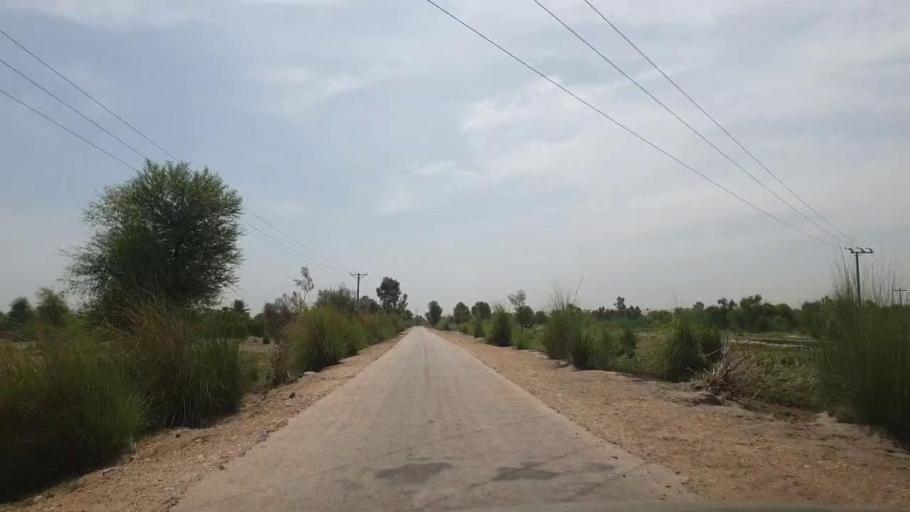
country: PK
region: Sindh
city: Kot Diji
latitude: 27.1120
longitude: 69.0187
